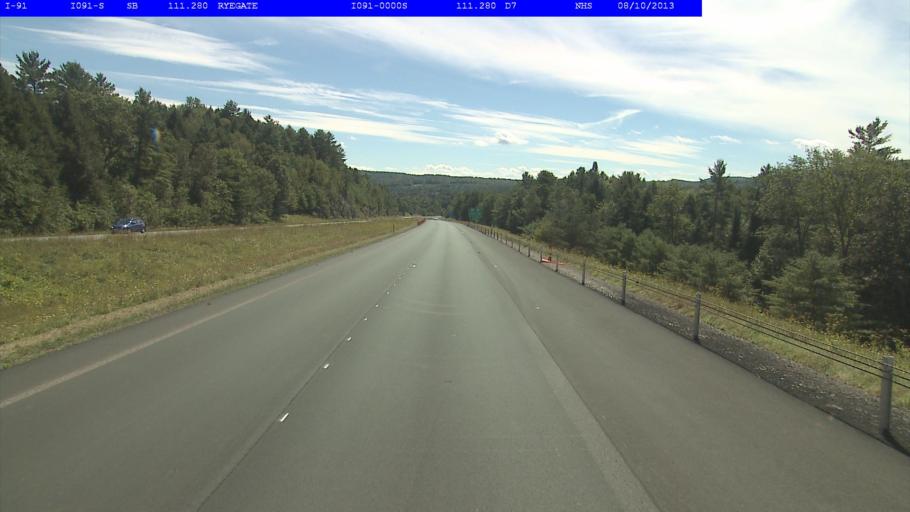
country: US
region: New Hampshire
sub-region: Grafton County
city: Woodsville
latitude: 44.1726
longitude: -72.0824
